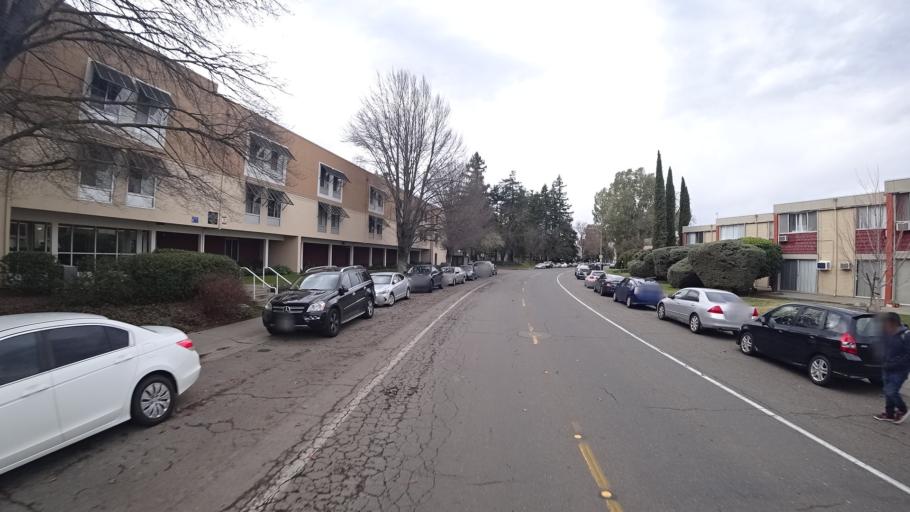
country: US
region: California
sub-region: Yolo County
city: Davis
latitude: 38.5480
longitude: -121.7635
